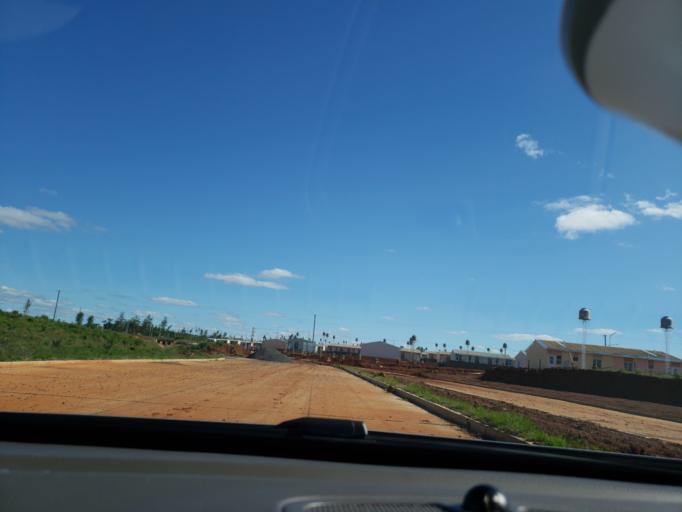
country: AR
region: Misiones
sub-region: Departamento de Capital
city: Posadas
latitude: -27.4113
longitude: -55.9892
